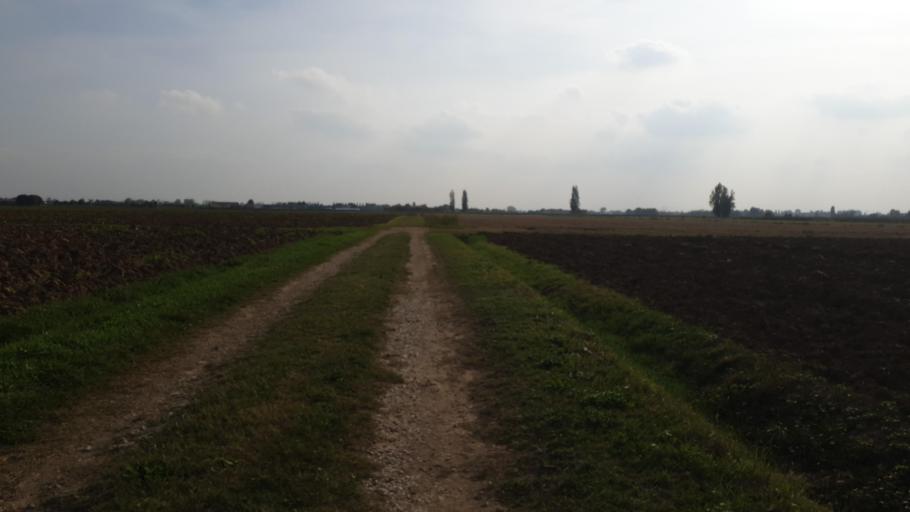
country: IT
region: Veneto
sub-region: Provincia di Padova
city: Ponte San Nicolo
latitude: 45.3404
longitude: 11.9280
